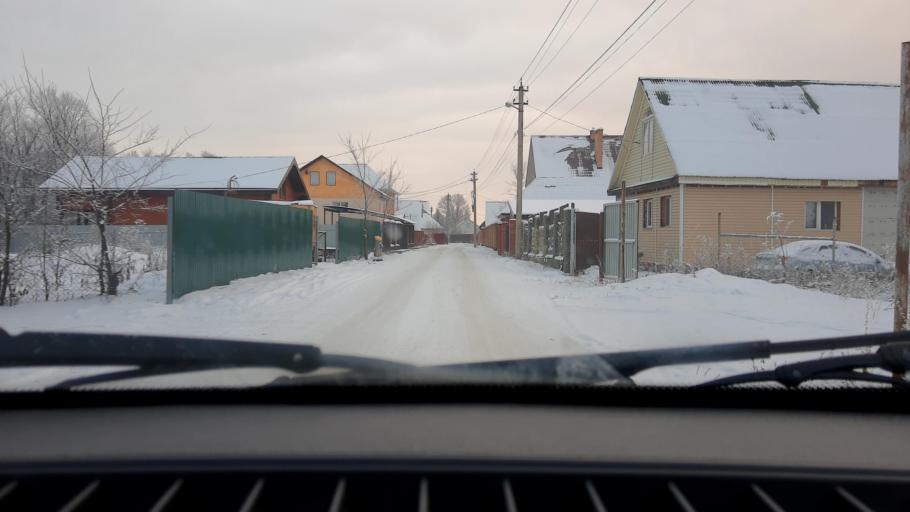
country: RU
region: Bashkortostan
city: Ufa
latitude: 54.6585
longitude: 55.9250
